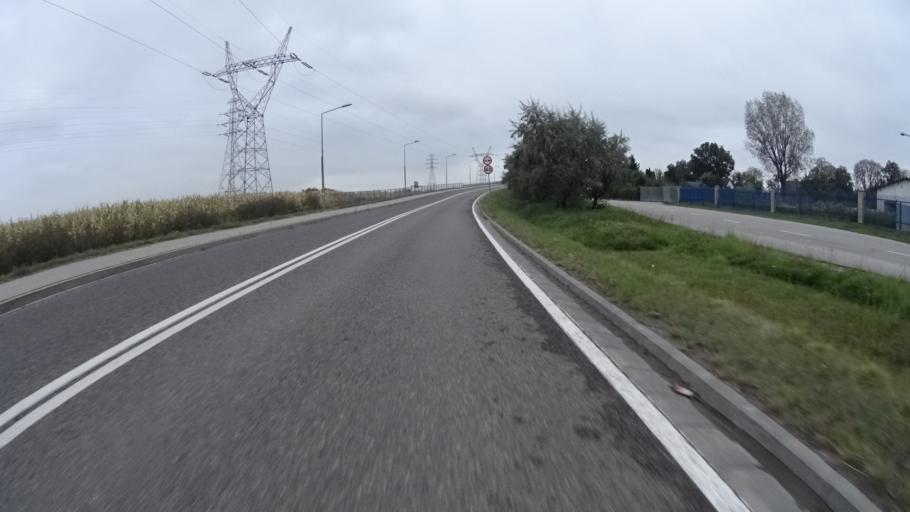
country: PL
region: Masovian Voivodeship
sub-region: Powiat warszawski zachodni
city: Babice
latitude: 52.2242
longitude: 20.8686
